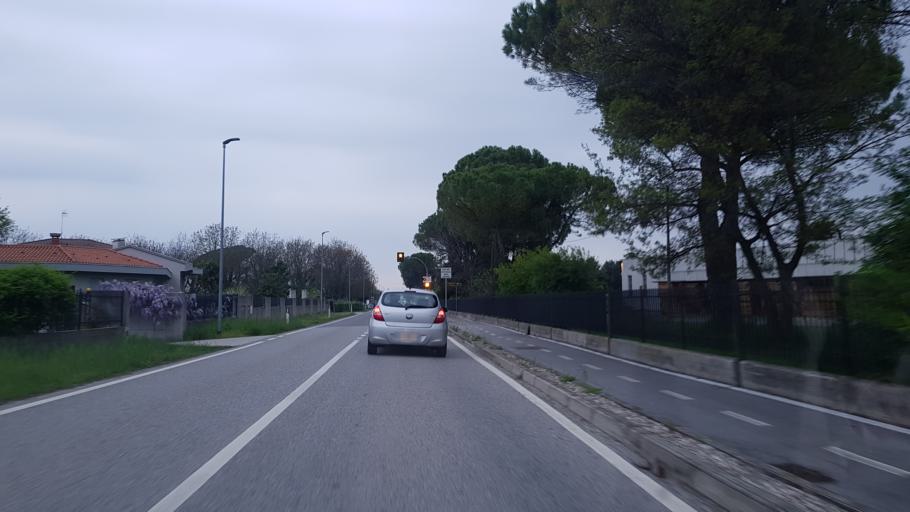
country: IT
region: Friuli Venezia Giulia
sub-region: Provincia di Udine
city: Visco
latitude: 45.8908
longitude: 13.3538
